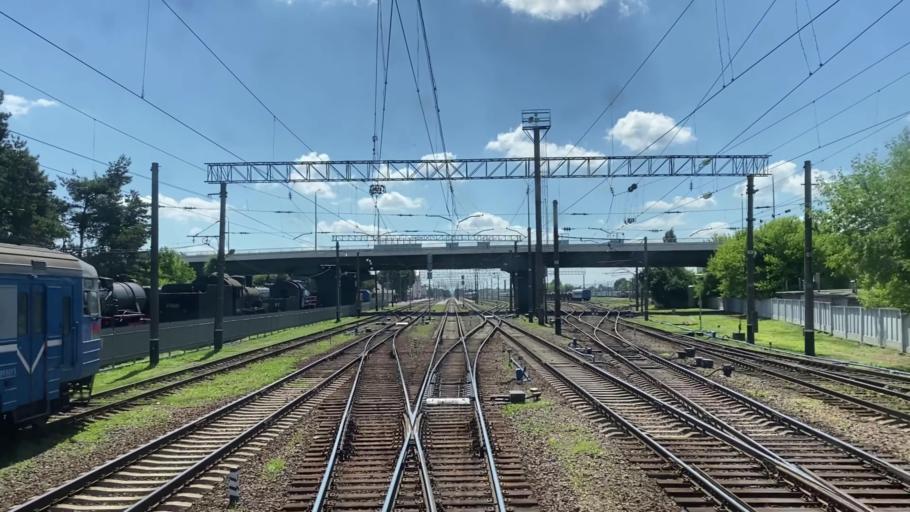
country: BY
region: Brest
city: Baranovichi
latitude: 53.1331
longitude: 26.0380
